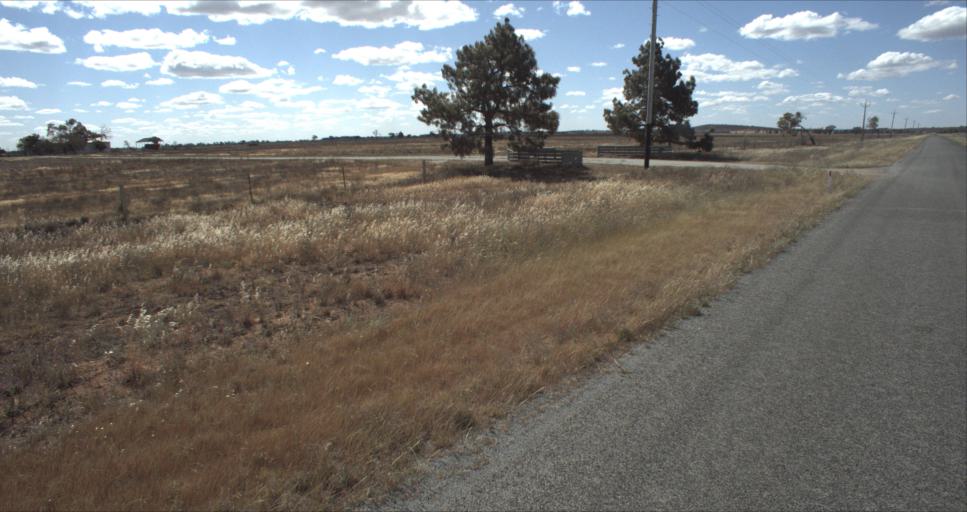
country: AU
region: New South Wales
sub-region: Leeton
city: Leeton
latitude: -34.4574
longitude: 146.2534
